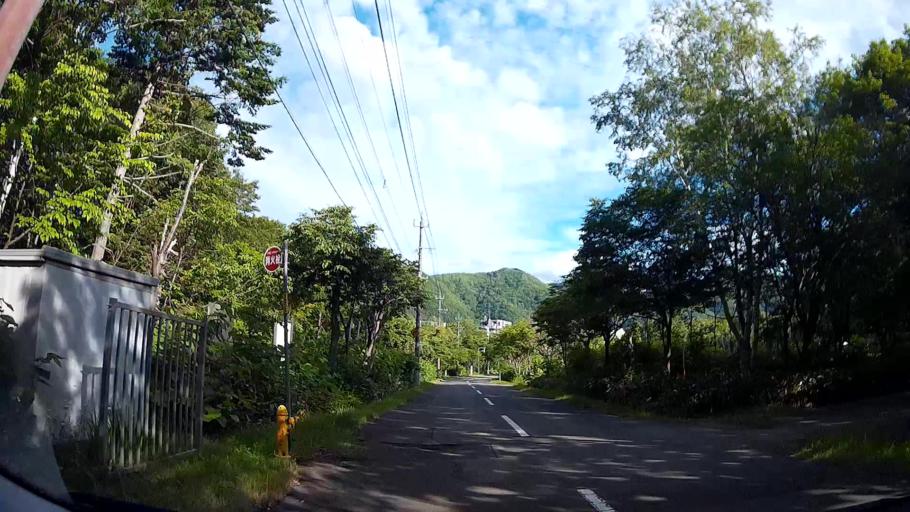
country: JP
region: Hokkaido
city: Sapporo
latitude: 42.9757
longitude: 141.1651
